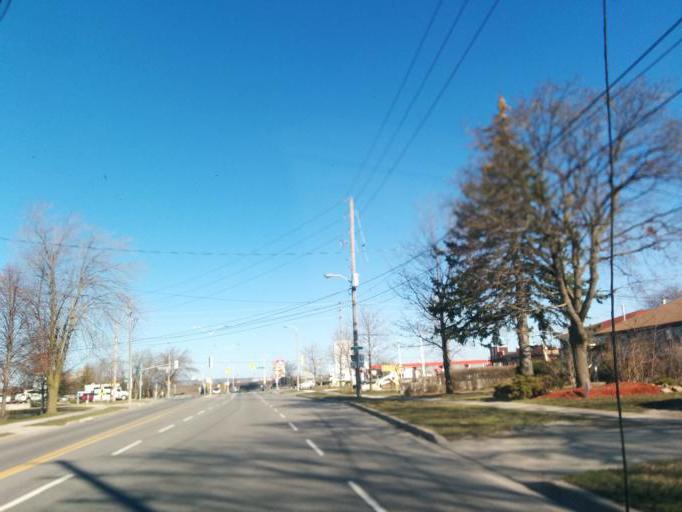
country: CA
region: Ontario
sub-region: Halton
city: Milton
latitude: 43.5206
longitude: -79.8928
